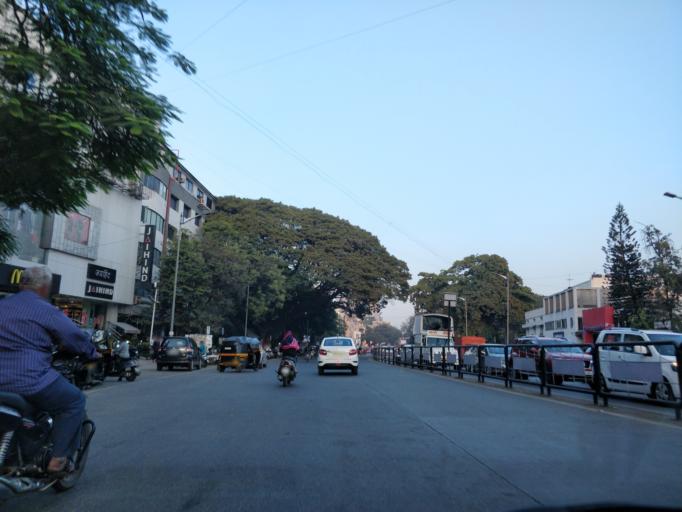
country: IN
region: Maharashtra
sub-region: Pune Division
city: Pune
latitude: 18.5044
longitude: 73.8214
